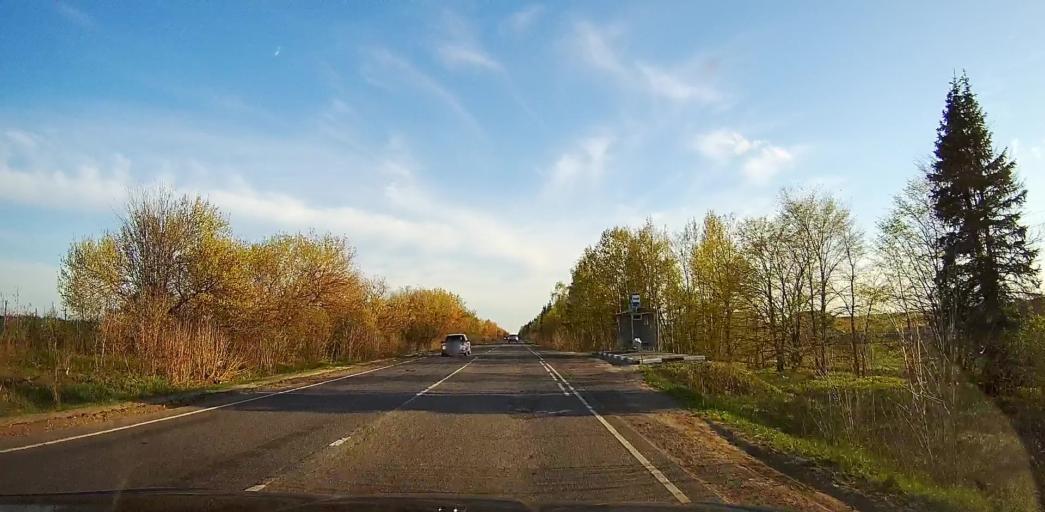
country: RU
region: Moskovskaya
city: Bronnitsy
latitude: 55.3192
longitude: 38.2174
